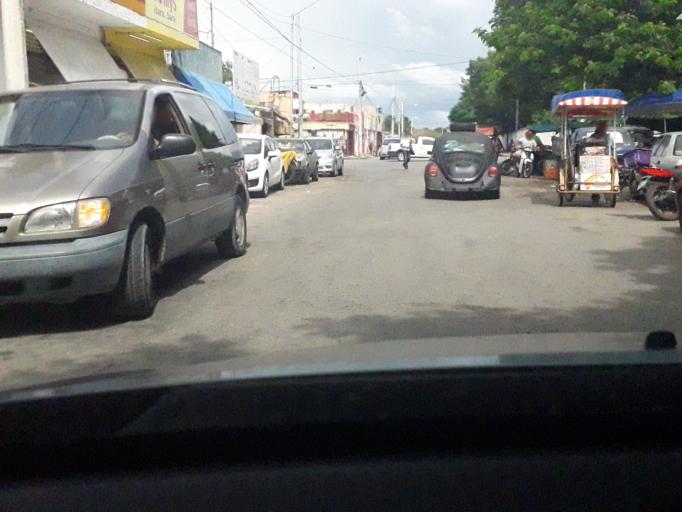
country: MX
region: Yucatan
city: Merida
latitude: 20.9698
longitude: -89.6581
